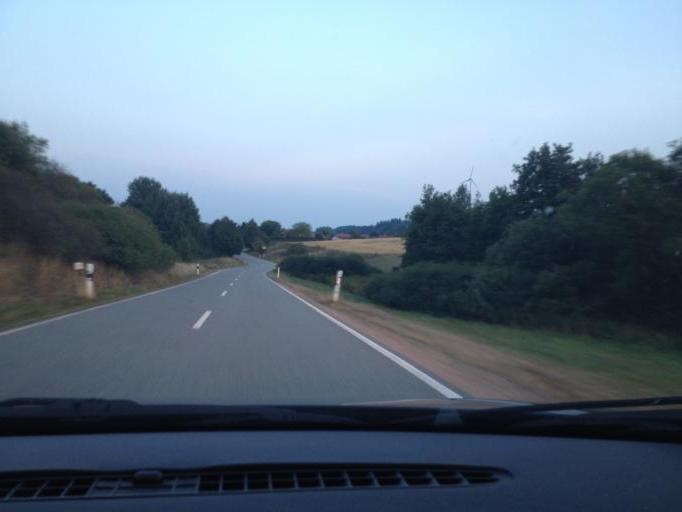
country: DE
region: Saarland
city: Nohfelden
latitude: 49.5594
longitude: 7.1547
